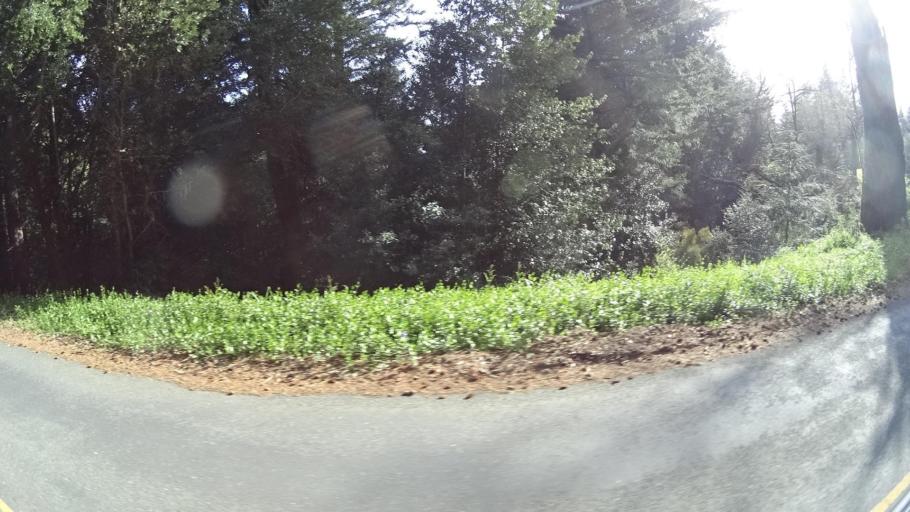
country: US
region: California
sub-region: Humboldt County
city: Blue Lake
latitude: 40.7229
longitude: -123.9440
